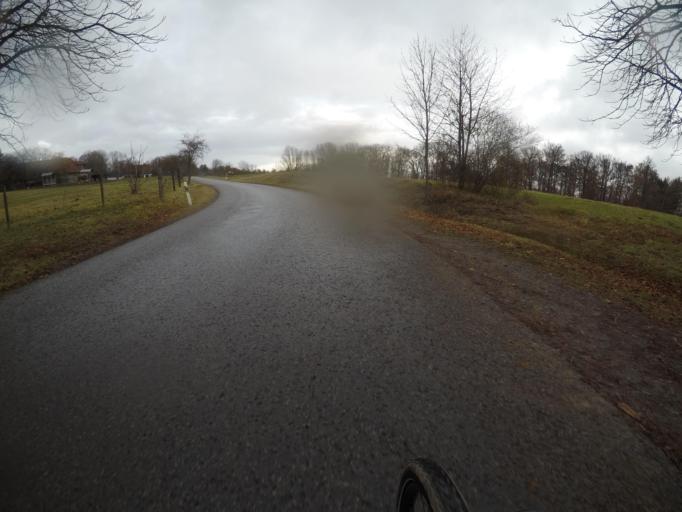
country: DE
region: Baden-Wuerttemberg
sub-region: Regierungsbezirk Stuttgart
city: Gerlingen
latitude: 48.7854
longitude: 9.0903
